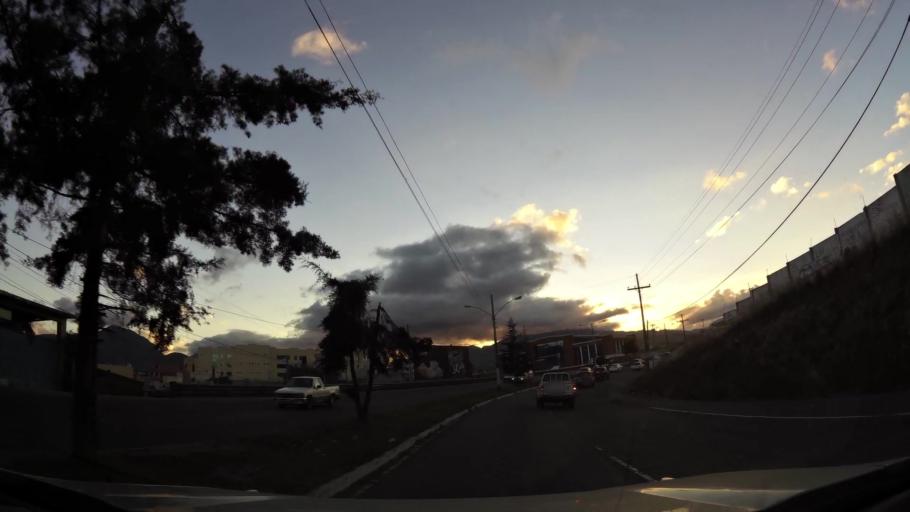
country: GT
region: Quetzaltenango
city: Quetzaltenango
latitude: 14.8584
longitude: -91.5100
